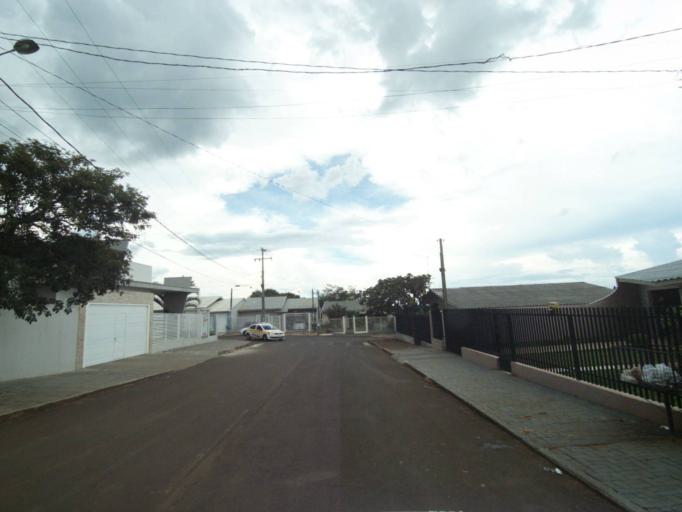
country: BR
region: Parana
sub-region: Guaraniacu
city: Guaraniacu
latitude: -25.0955
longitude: -52.8724
